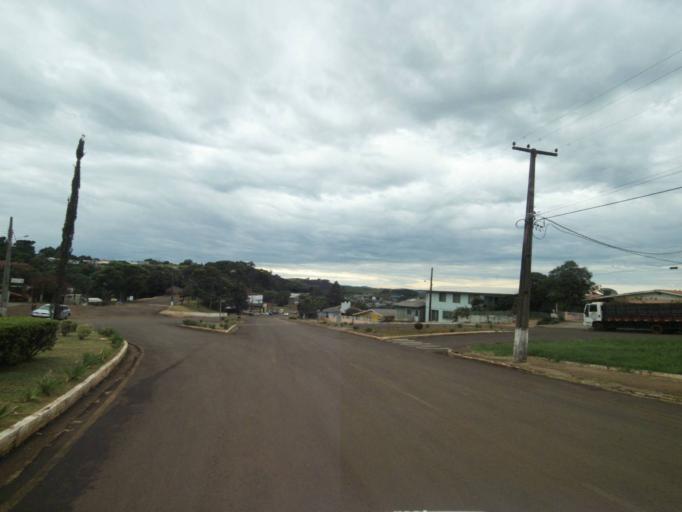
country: BR
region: Parana
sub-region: Guaraniacu
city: Guaraniacu
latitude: -25.1039
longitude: -52.8619
